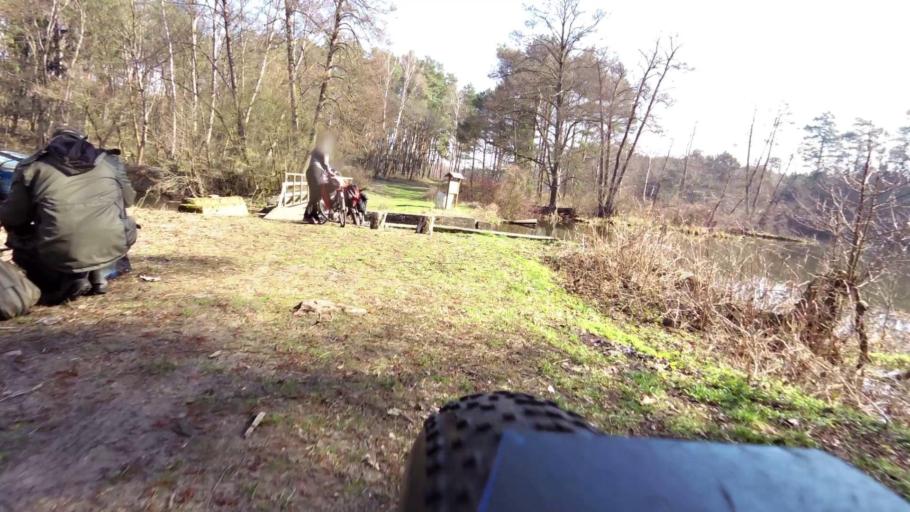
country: PL
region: Lubusz
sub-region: Powiat krosnienski
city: Maszewo
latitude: 52.2120
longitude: 14.9430
